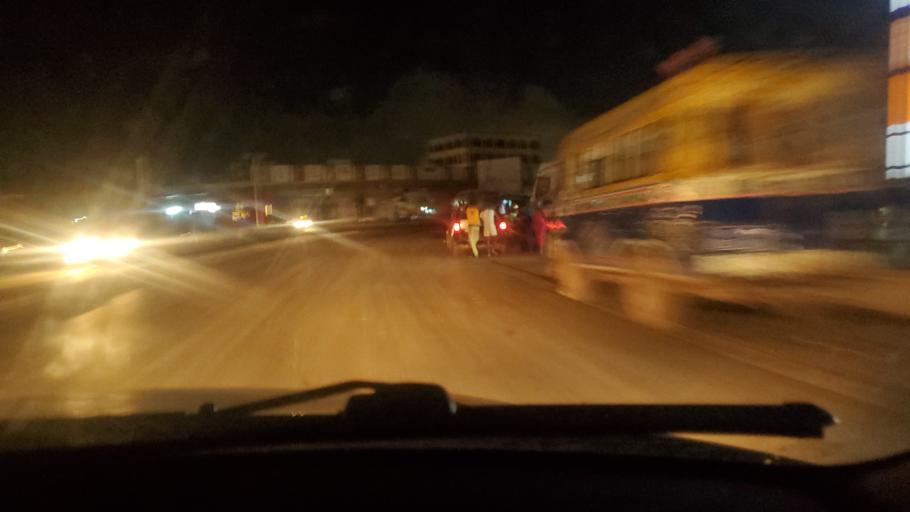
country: SN
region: Dakar
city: Pikine
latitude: 14.7466
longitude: -17.3774
